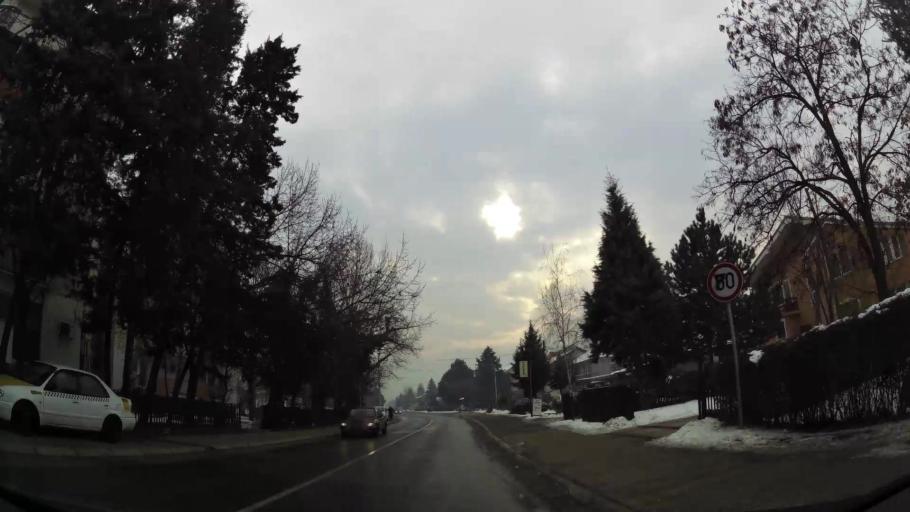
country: MK
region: Saraj
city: Saraj
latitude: 42.0213
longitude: 21.3516
